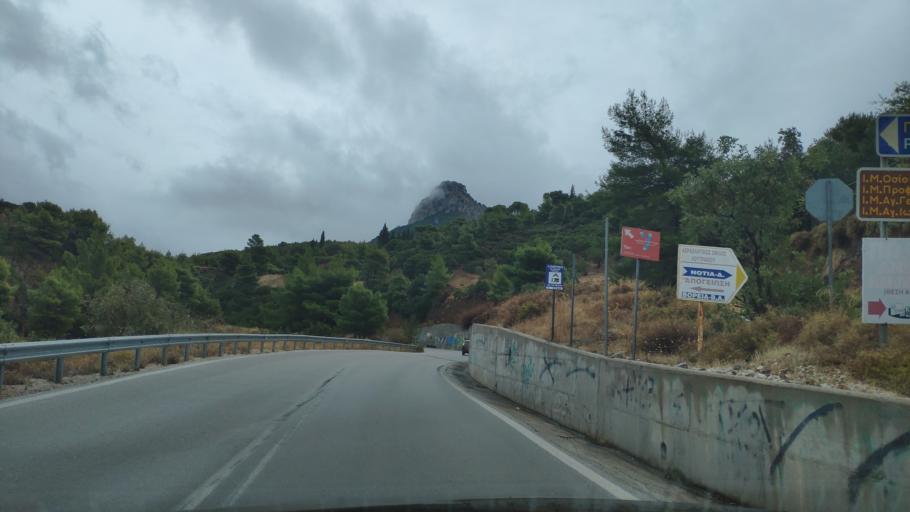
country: GR
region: Peloponnese
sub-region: Nomos Korinthias
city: Perachora
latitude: 38.0075
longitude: 22.9415
